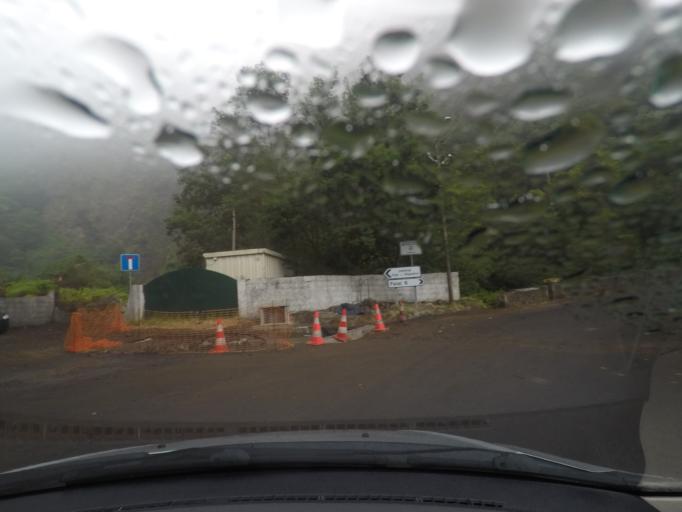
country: PT
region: Madeira
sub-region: Santana
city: Santana
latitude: 32.7540
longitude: -16.8806
